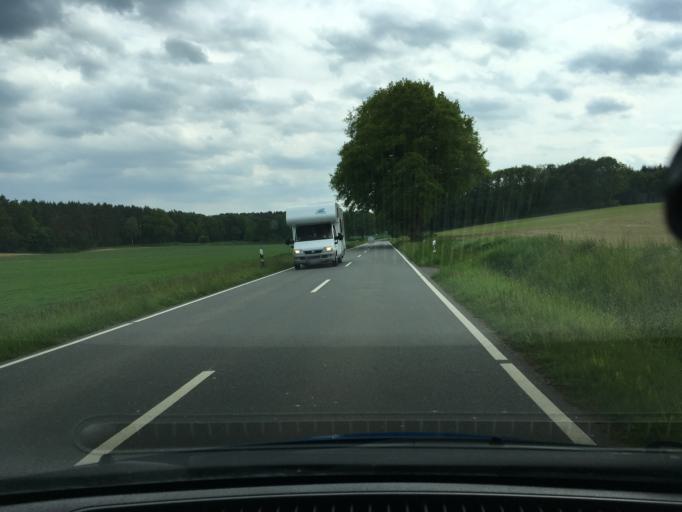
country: DE
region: Lower Saxony
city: Betzendorf
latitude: 53.1220
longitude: 10.3098
